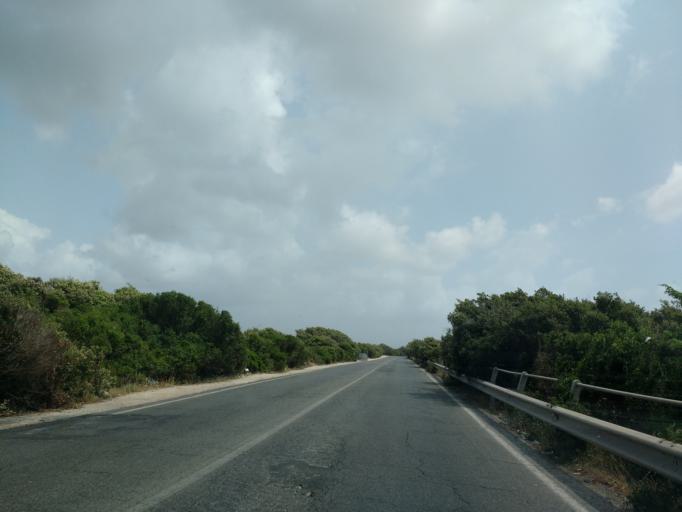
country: IT
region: Latium
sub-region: Citta metropolitana di Roma Capitale
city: Torvaianica
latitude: 41.6644
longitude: 12.4060
